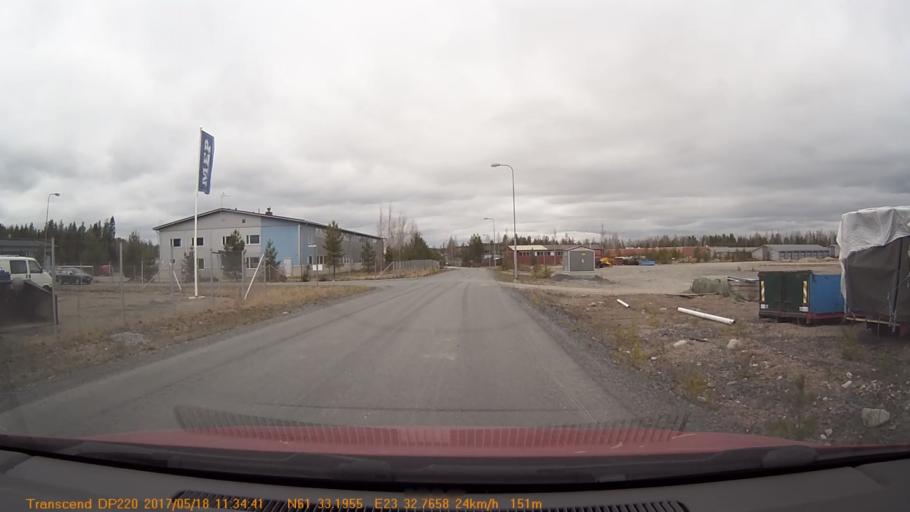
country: FI
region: Pirkanmaa
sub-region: Tampere
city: Yloejaervi
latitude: 61.5531
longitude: 23.5463
